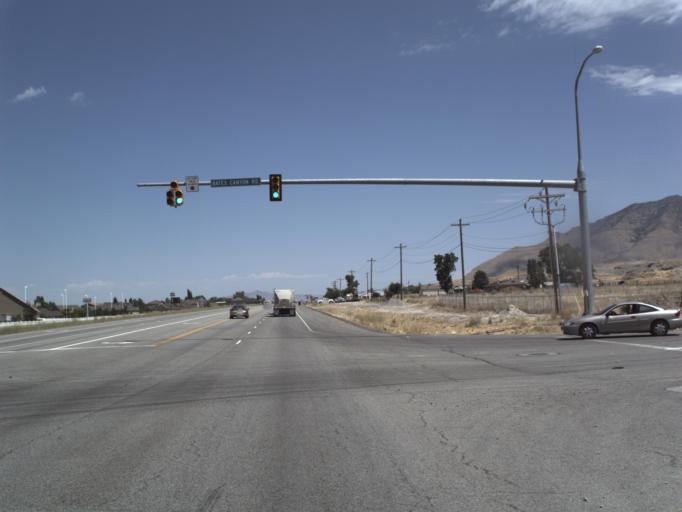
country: US
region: Utah
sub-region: Tooele County
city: Erda
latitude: 40.6206
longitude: -112.2938
